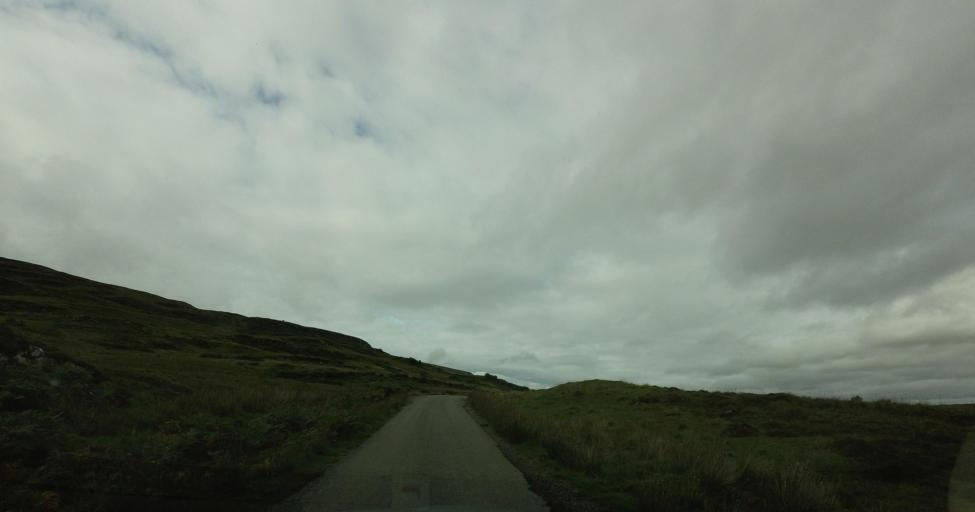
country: GB
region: Scotland
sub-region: Highland
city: Portree
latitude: 57.4150
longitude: -6.2171
